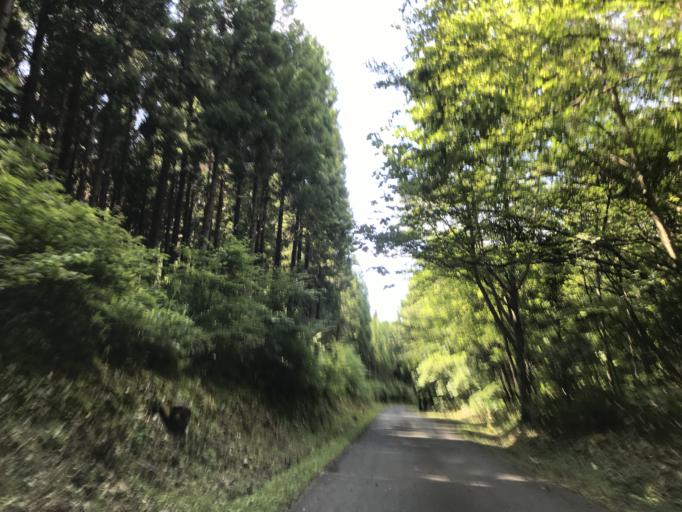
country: JP
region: Iwate
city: Ichinoseki
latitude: 38.9234
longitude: 140.9568
